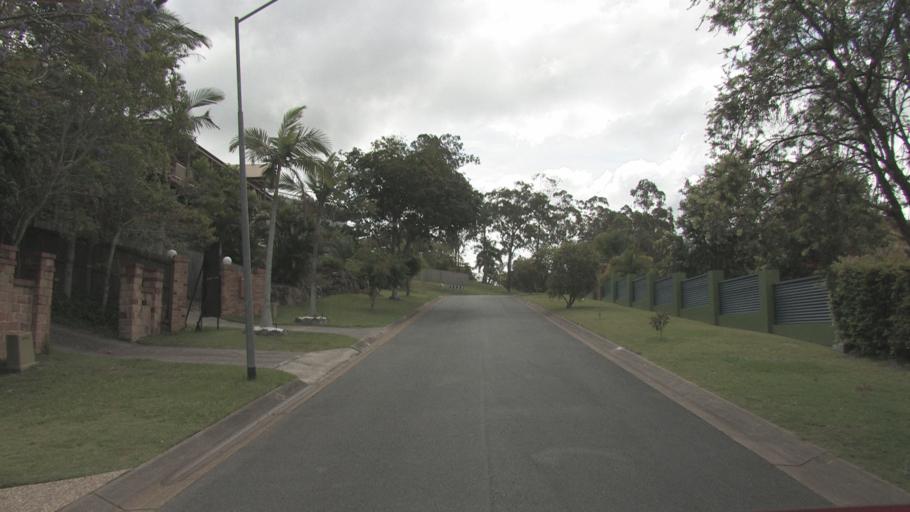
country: AU
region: Queensland
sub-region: Logan
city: Beenleigh
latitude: -27.6666
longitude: 153.2005
